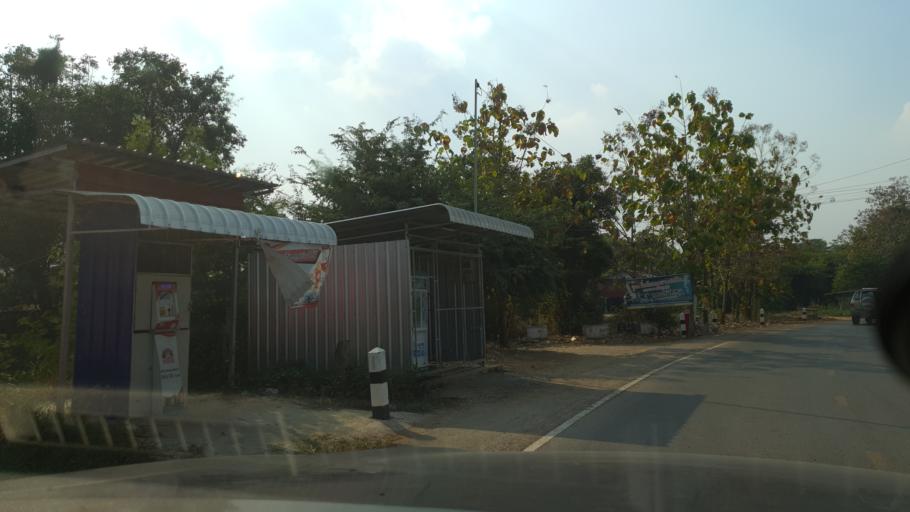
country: TH
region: Sukhothai
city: Ban Dan Lan Hoi
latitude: 17.1135
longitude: 99.5408
